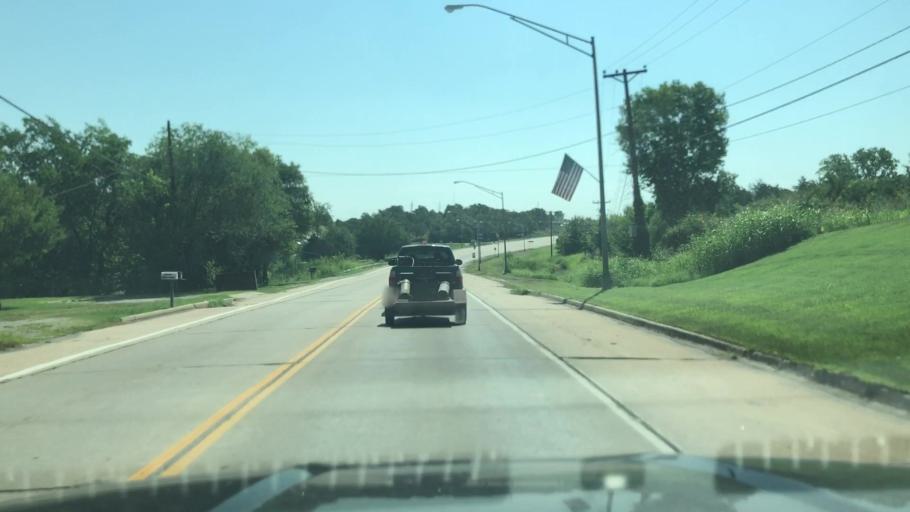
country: US
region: Oklahoma
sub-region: Creek County
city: Drumright
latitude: 35.9885
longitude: -96.5901
